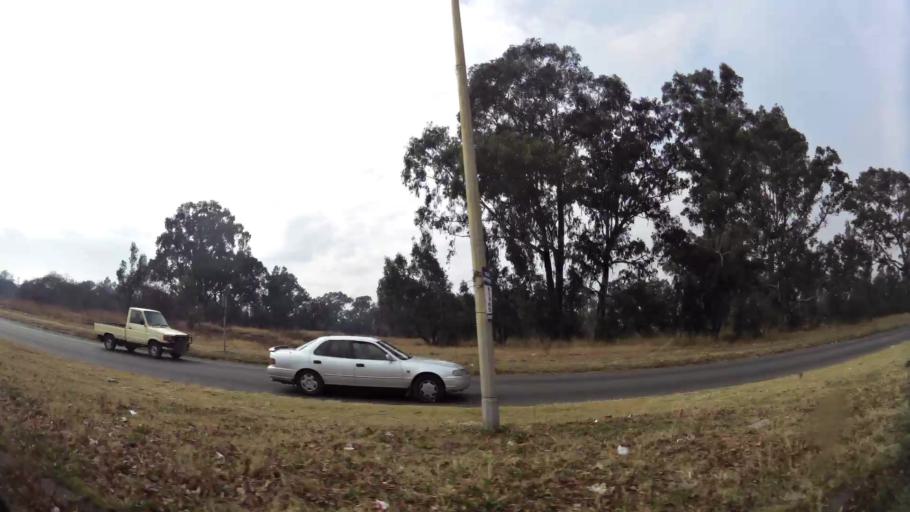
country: ZA
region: Gauteng
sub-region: Sedibeng District Municipality
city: Vanderbijlpark
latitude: -26.6751
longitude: 27.8373
